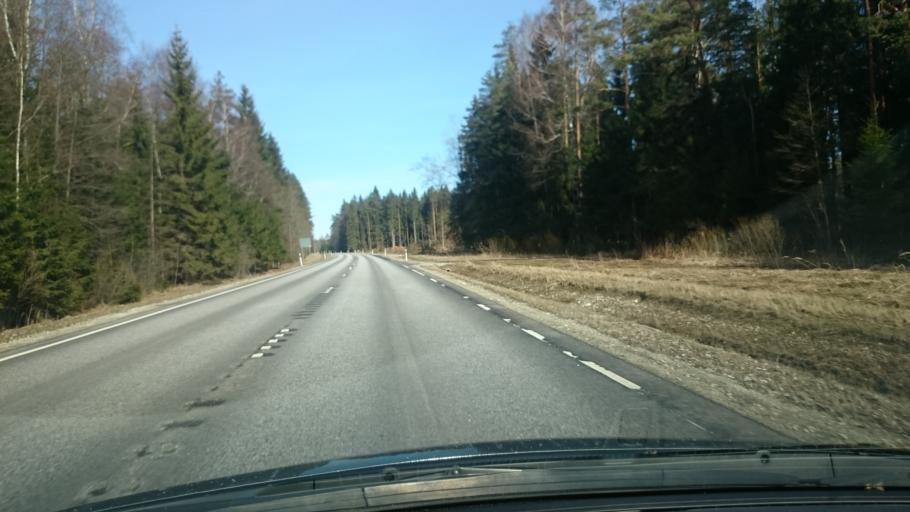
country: EE
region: Jaervamaa
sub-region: Tueri vald
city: Sarevere
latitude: 58.6996
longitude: 25.2591
